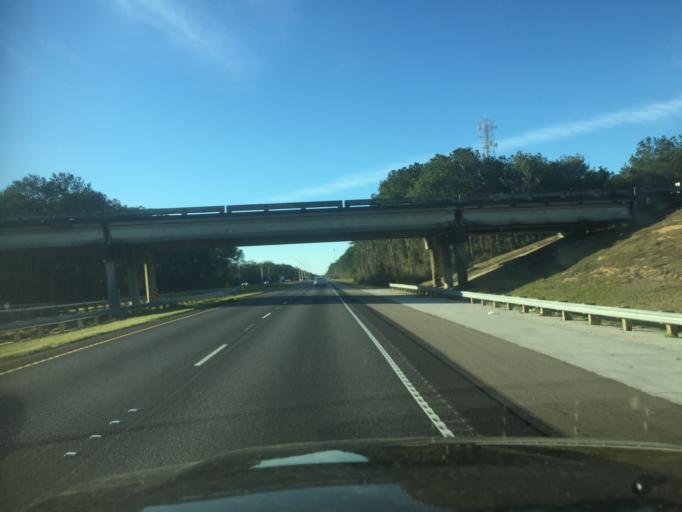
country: US
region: Louisiana
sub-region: Saint Tammany Parish
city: Lacombe
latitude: 30.3522
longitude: -89.9200
